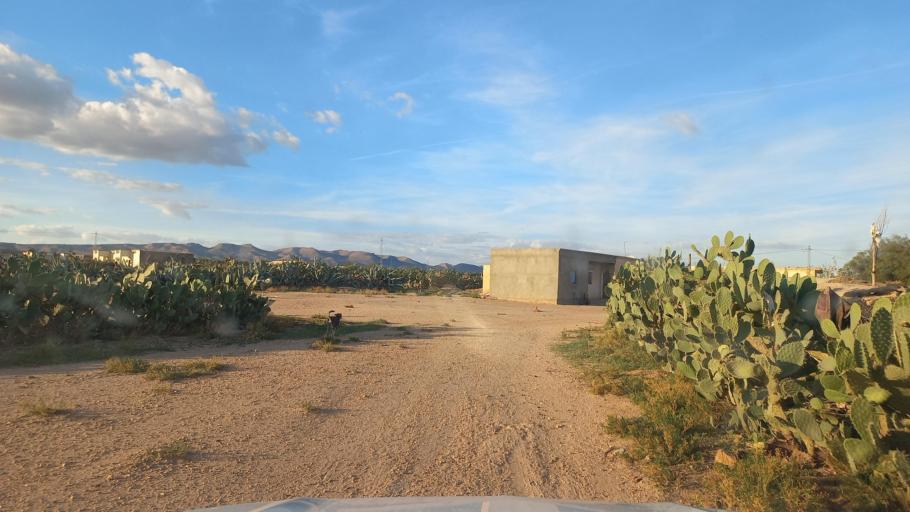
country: TN
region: Al Qasrayn
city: Sbiba
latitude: 35.3528
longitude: 9.0344
